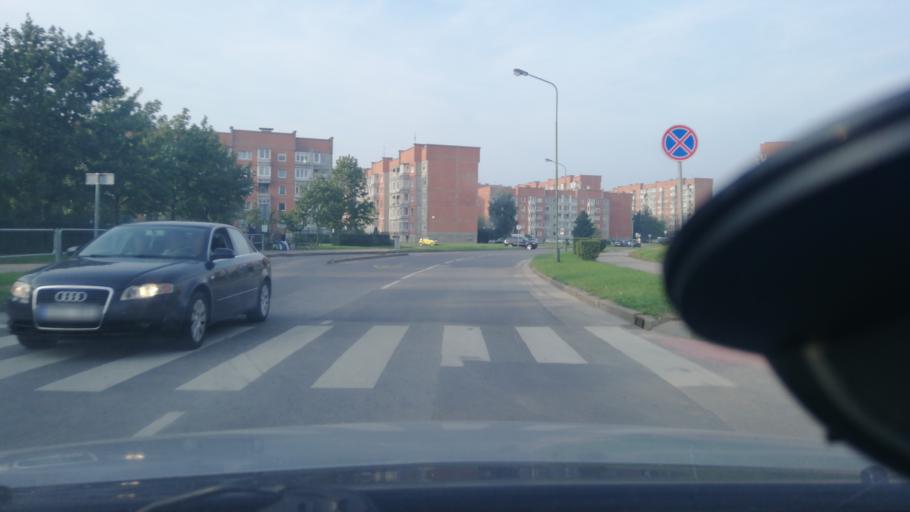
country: LT
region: Klaipedos apskritis
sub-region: Klaipeda
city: Klaipeda
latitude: 55.6643
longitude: 21.2002
